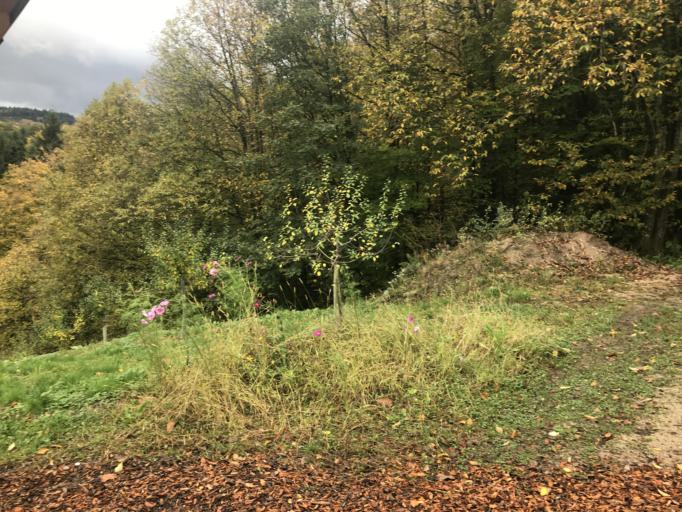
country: DE
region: Baden-Wuerttemberg
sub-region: Freiburg Region
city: Kappelrodeck
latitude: 48.5712
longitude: 8.0901
